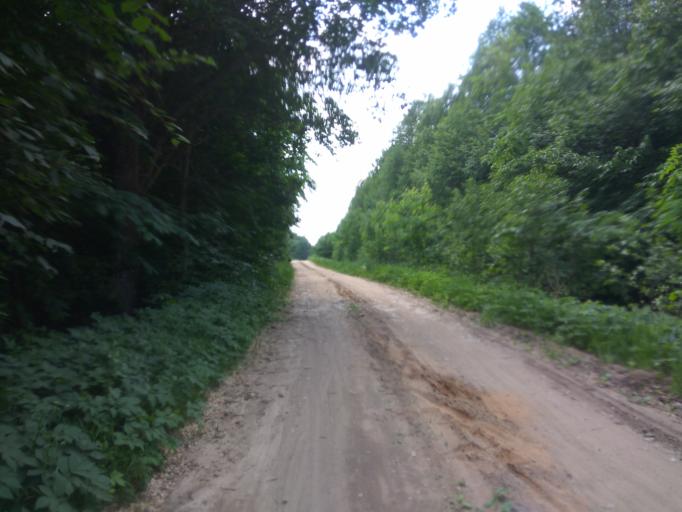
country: LV
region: Kuldigas Rajons
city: Kuldiga
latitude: 56.8898
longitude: 21.9730
